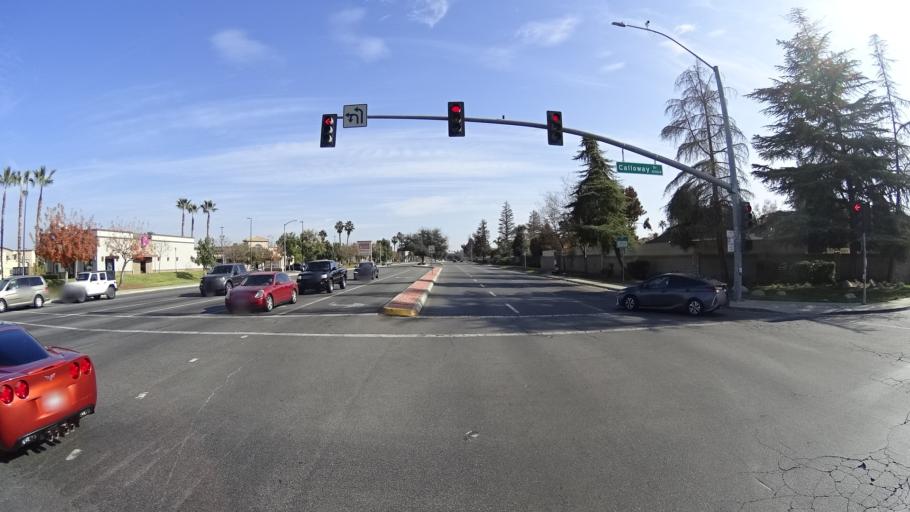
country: US
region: California
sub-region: Kern County
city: Greenacres
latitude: 35.3980
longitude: -119.1100
